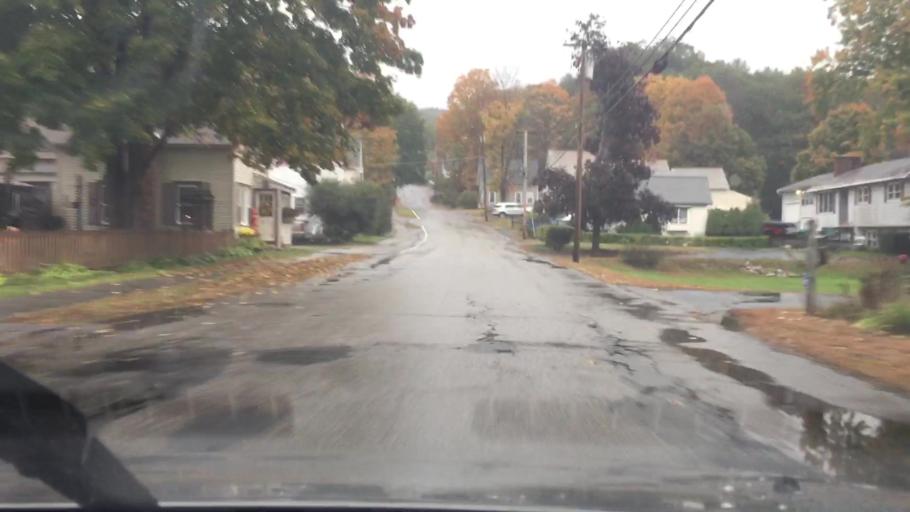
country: US
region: New Hampshire
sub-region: Cheshire County
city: Keene
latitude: 42.9446
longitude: -72.2711
